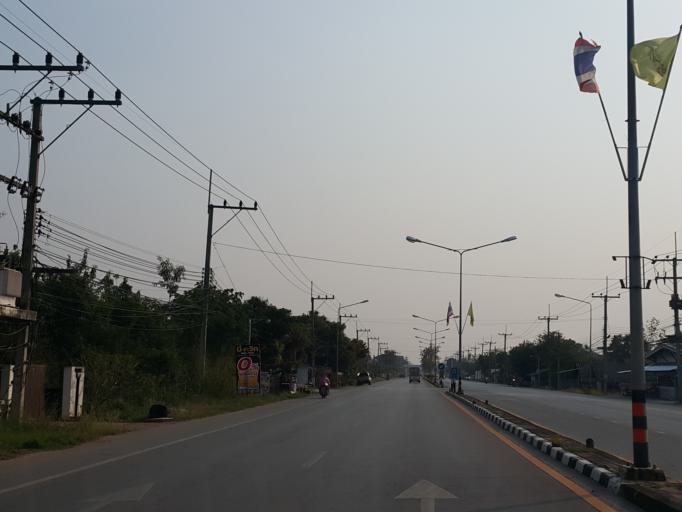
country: TH
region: Lampang
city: Lampang
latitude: 18.3263
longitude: 99.5253
